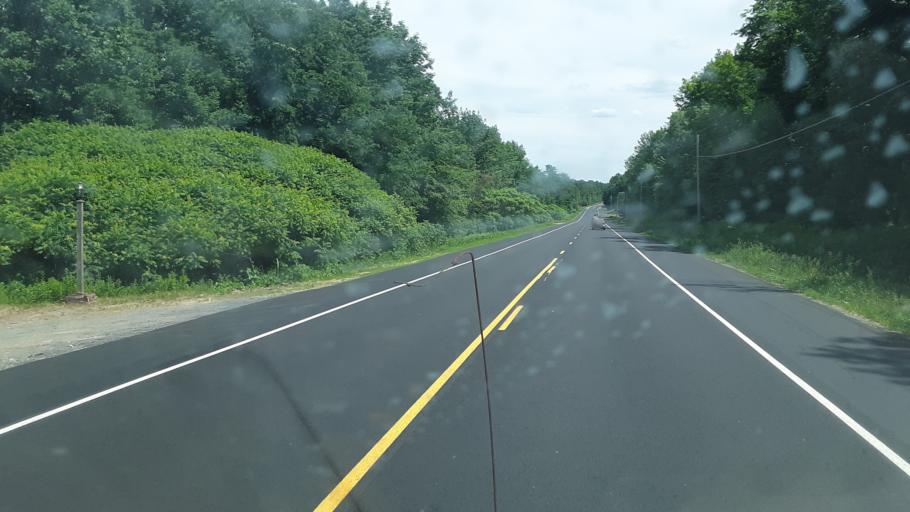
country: US
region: Maine
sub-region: Somerset County
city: Norridgewock
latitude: 44.6629
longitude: -69.7077
